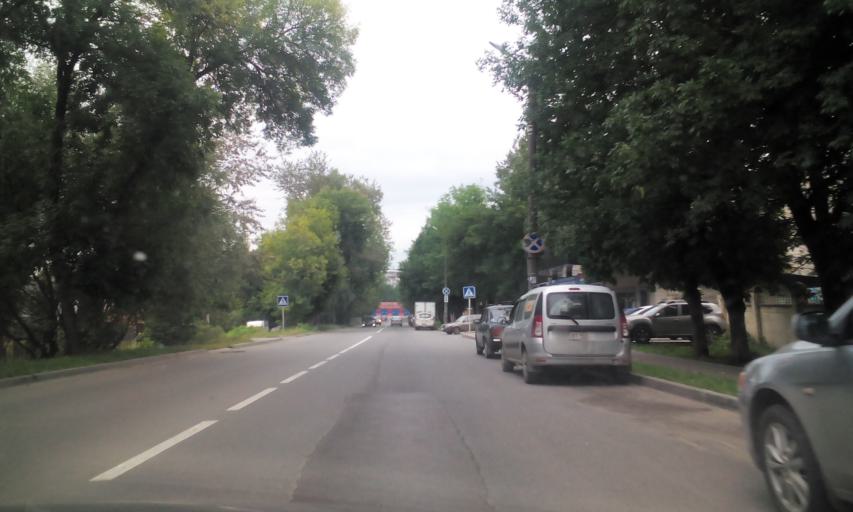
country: RU
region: Kaluga
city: Kaluga
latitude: 54.5126
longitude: 36.2912
